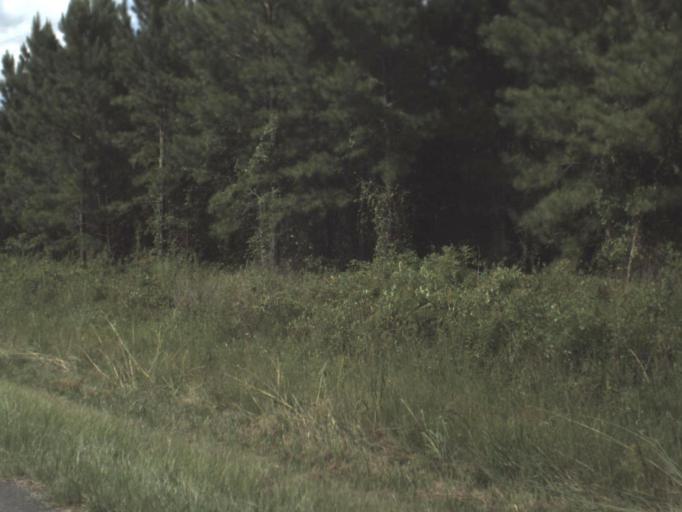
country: US
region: Florida
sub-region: Taylor County
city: Perry
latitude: 30.3621
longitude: -83.6562
